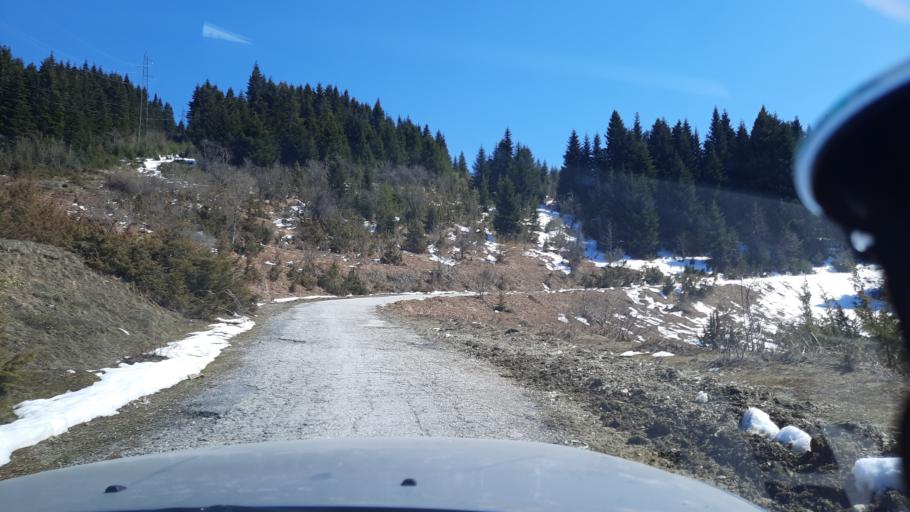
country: MK
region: Gostivar
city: Vrutok
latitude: 41.7148
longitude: 20.7257
